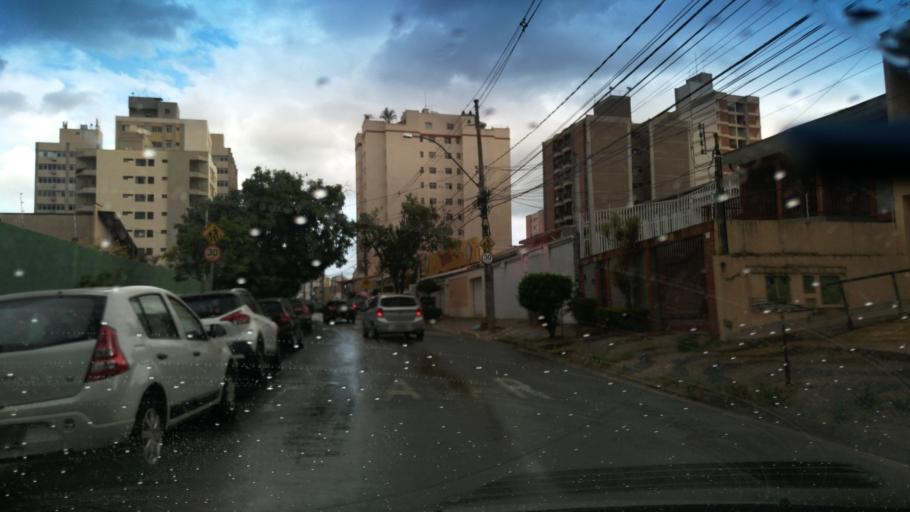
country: BR
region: Sao Paulo
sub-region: Campinas
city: Campinas
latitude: -22.9077
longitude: -47.0463
